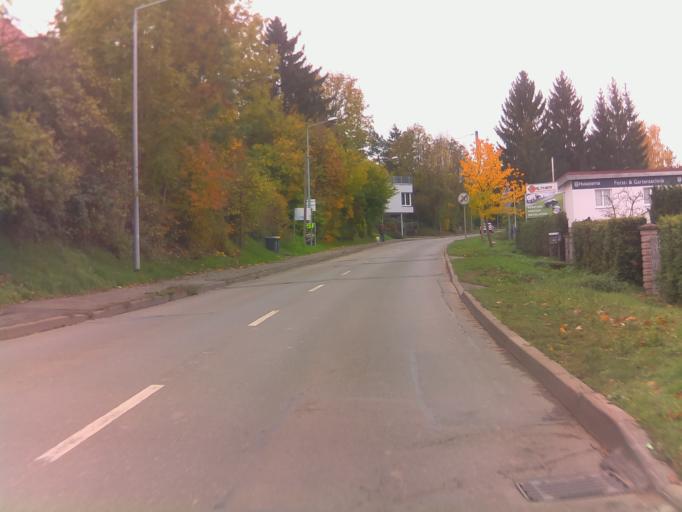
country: DE
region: Thuringia
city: Arnstadt
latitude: 50.8281
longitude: 10.9594
